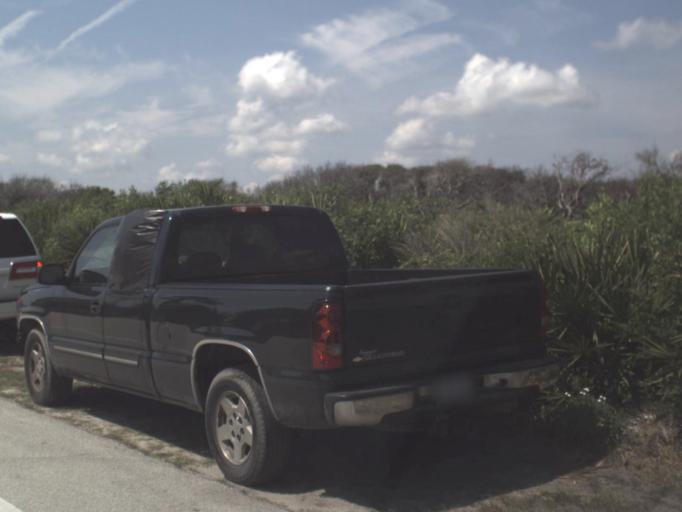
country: US
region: Florida
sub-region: Saint Johns County
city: Villano Beach
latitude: 30.0581
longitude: -81.3318
